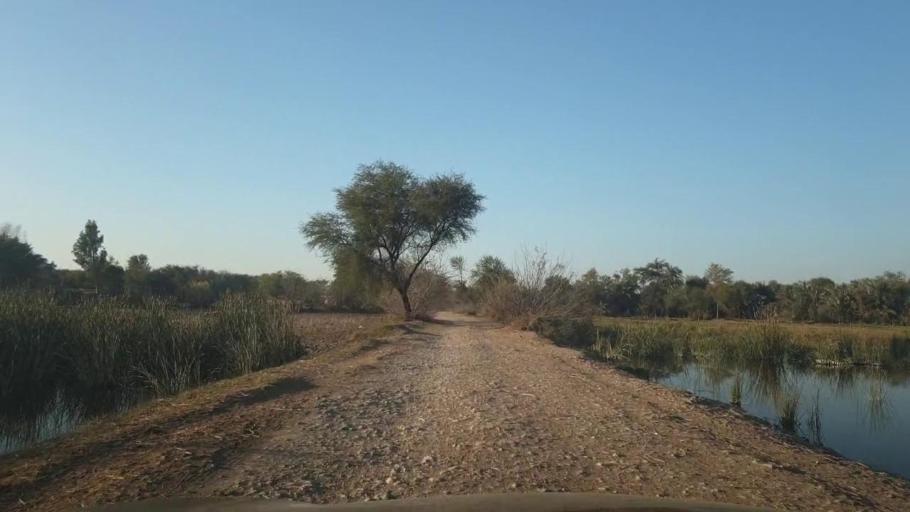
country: PK
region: Sindh
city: Mirpur Mathelo
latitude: 28.0036
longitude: 69.4663
